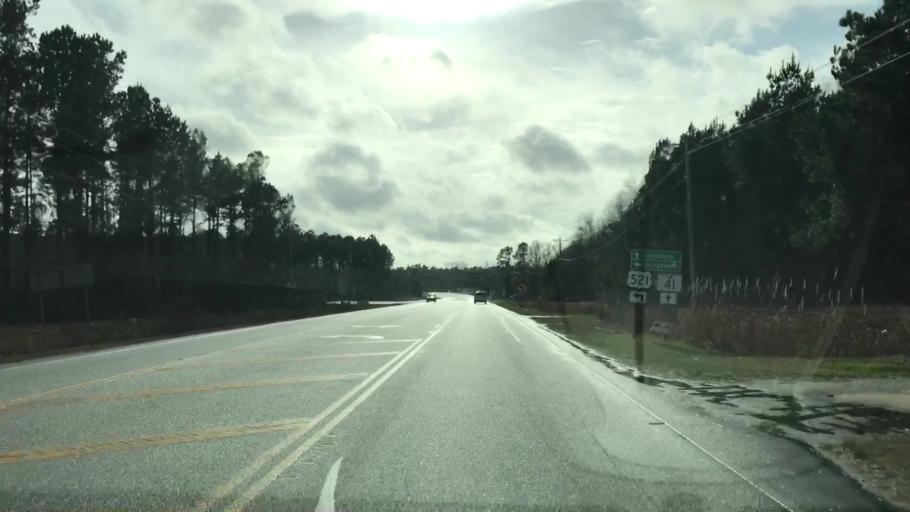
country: US
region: South Carolina
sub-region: Williamsburg County
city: Andrews
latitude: 33.4457
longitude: -79.5880
